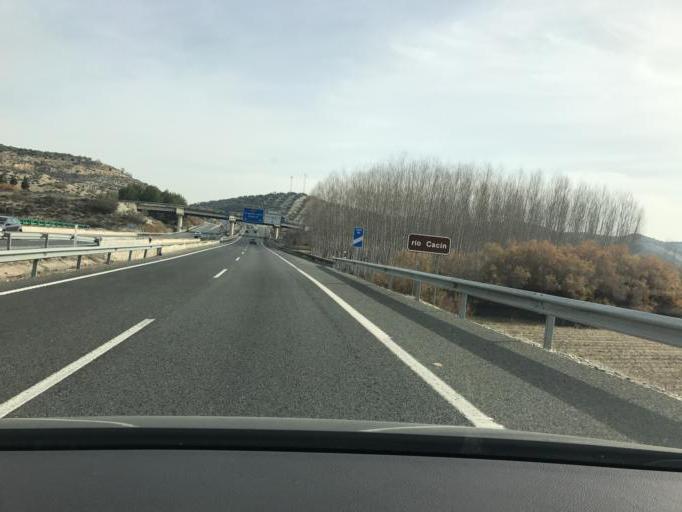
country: ES
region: Andalusia
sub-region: Provincia de Granada
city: Villanueva de Mesia
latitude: 37.1930
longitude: -4.0035
